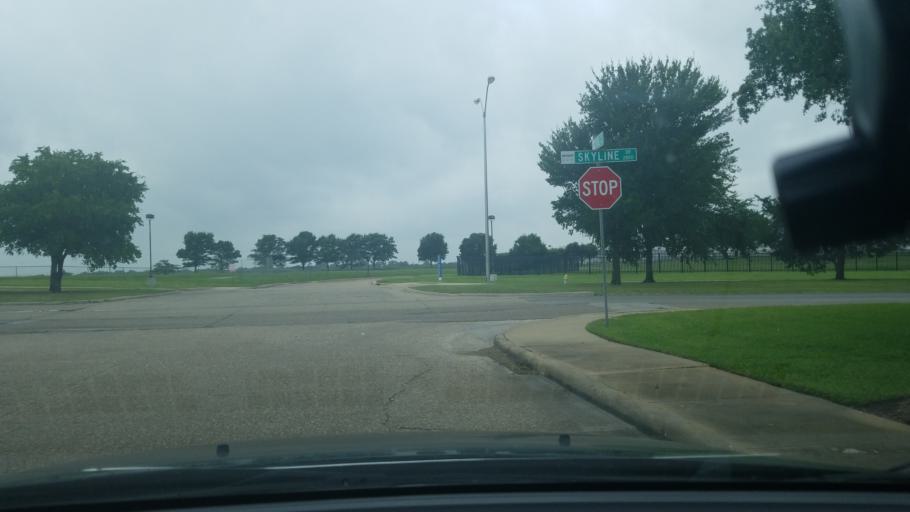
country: US
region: Texas
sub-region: Dallas County
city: Mesquite
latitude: 32.7808
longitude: -96.6396
